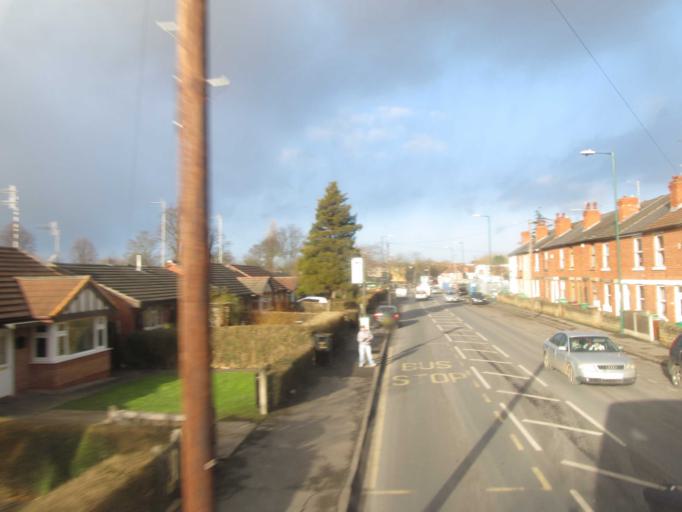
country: GB
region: England
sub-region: Nottinghamshire
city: Hucknall
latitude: 52.9928
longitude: -1.1981
